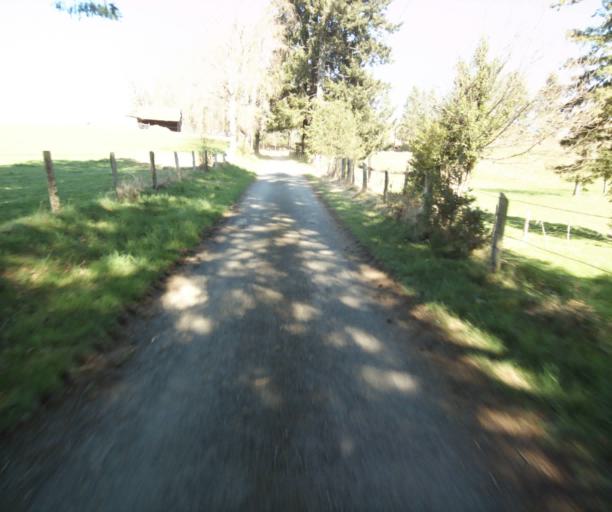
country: FR
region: Limousin
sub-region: Departement de la Correze
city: Saint-Clement
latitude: 45.3547
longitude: 1.6536
